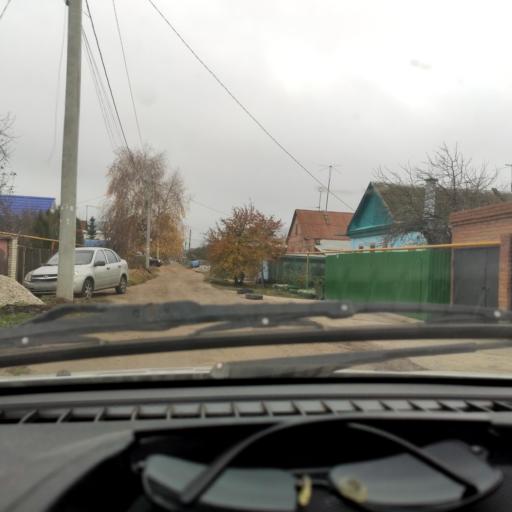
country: RU
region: Samara
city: Tol'yatti
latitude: 53.5401
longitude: 49.4216
